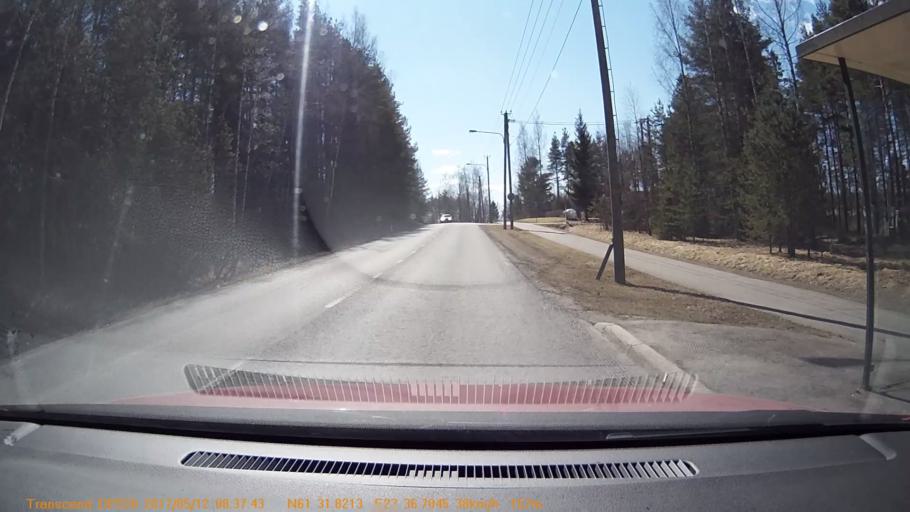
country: FI
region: Pirkanmaa
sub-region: Tampere
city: Yloejaervi
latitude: 61.5304
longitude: 23.6116
